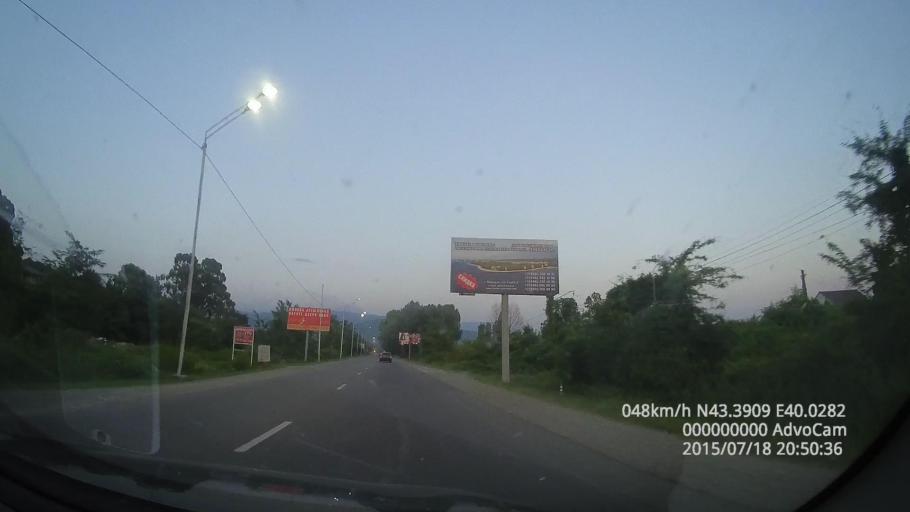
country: GE
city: Gantiadi
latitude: 43.3908
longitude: 40.0294
